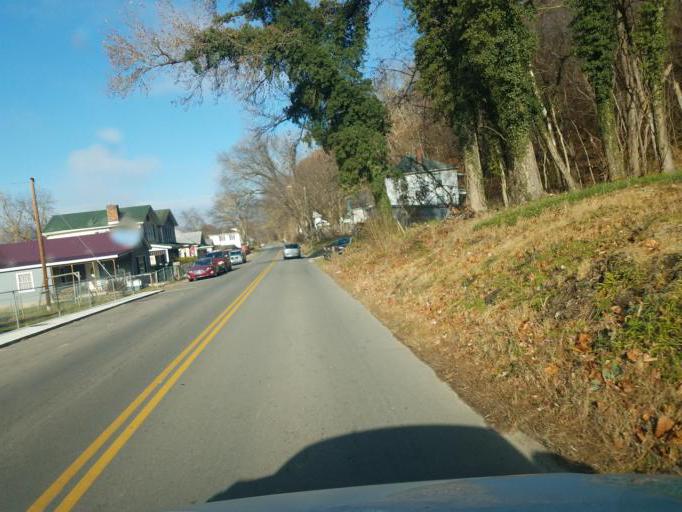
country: US
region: Ohio
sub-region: Scioto County
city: Sciotodale
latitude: 38.7534
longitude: -82.8783
